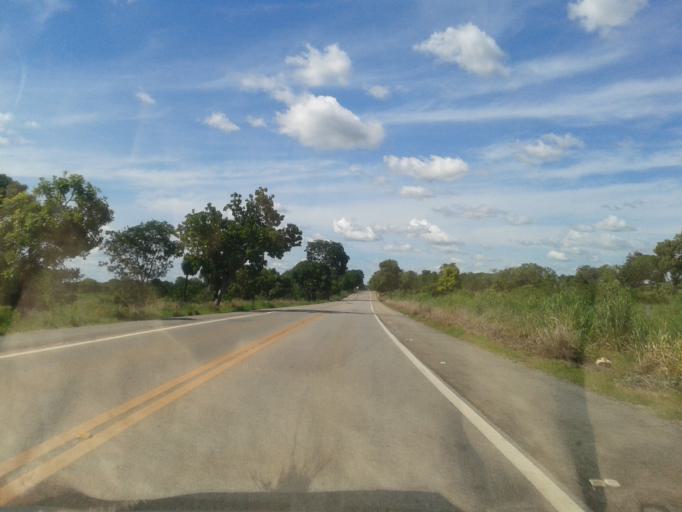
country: BR
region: Goias
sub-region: Itapuranga
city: Itapuranga
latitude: -15.4212
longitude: -50.3766
